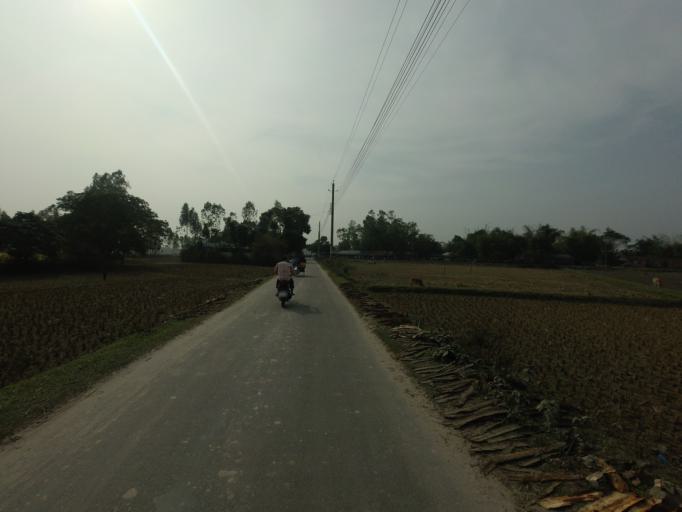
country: BD
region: Rajshahi
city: Saidpur
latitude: 25.9202
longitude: 88.8328
